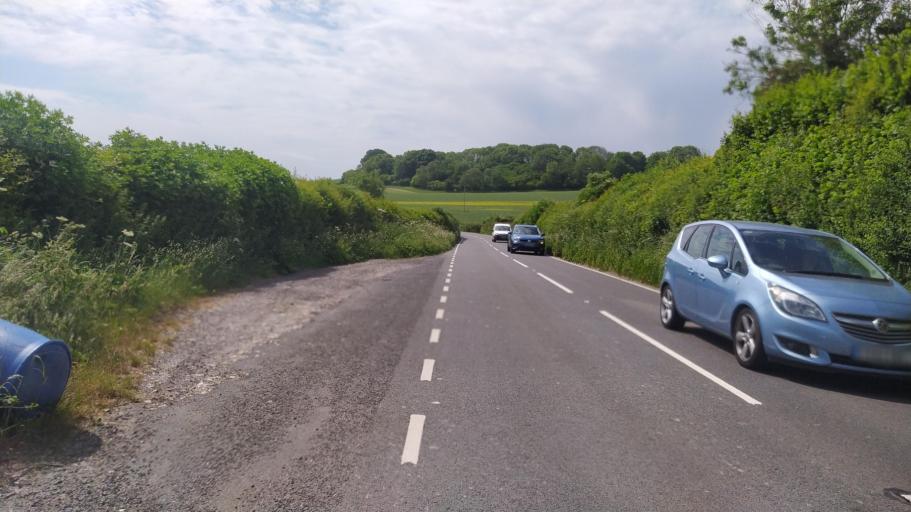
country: GB
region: England
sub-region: Dorset
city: Dorchester
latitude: 50.7931
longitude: -2.4786
